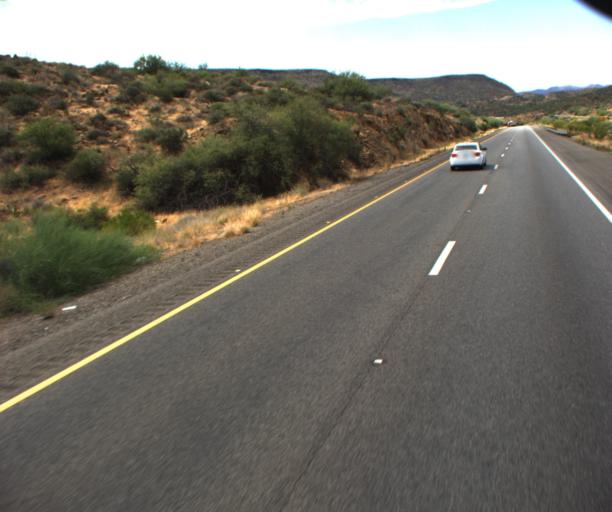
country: US
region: Arizona
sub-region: Yavapai County
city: Black Canyon City
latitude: 34.1477
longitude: -112.1496
